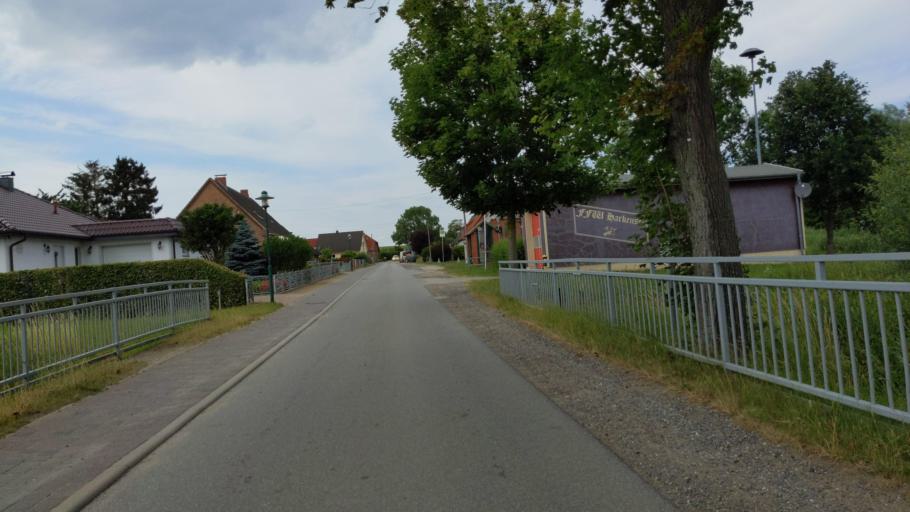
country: DE
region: Mecklenburg-Vorpommern
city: Dassow
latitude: 53.9577
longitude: 10.9753
